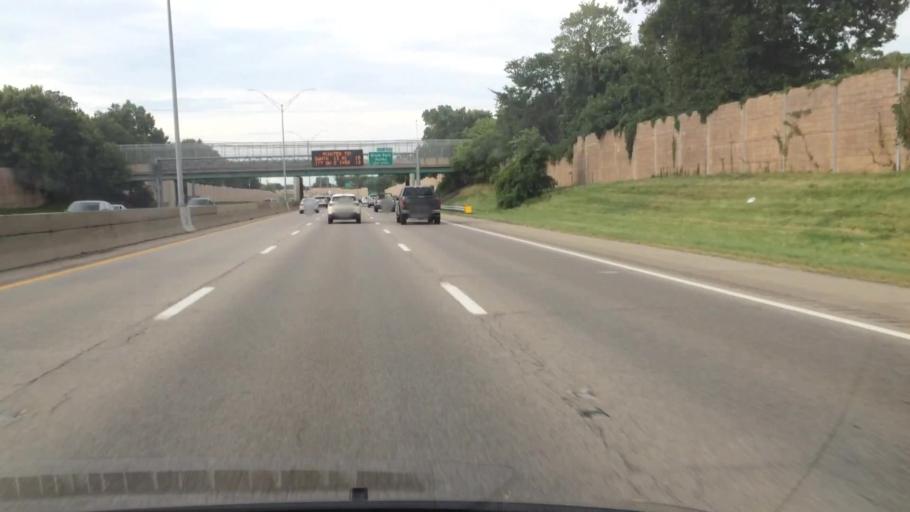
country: US
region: Ohio
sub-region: Cuyahoga County
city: Brook Park
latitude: 41.3874
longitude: -81.8169
